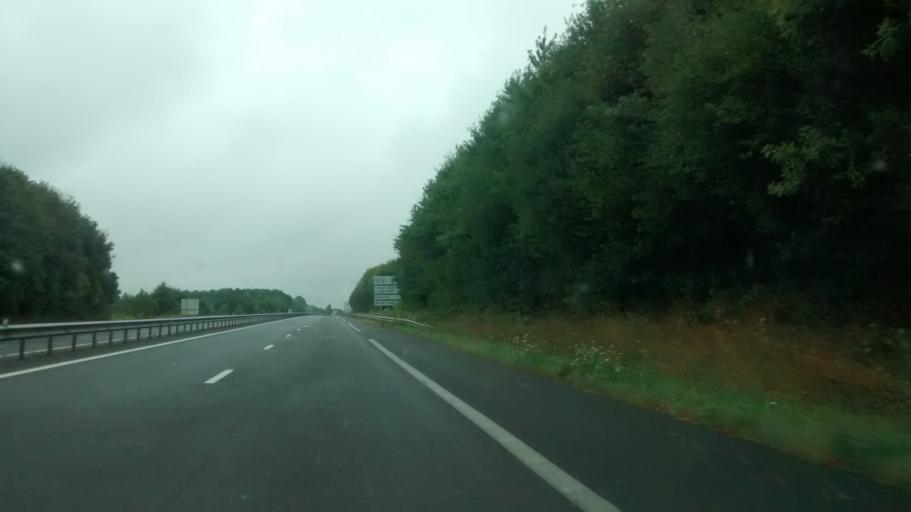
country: FR
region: Brittany
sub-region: Departement d'Ille-et-Vilaine
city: Saint-Etienne-en-Cogles
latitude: 48.4498
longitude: -1.3259
